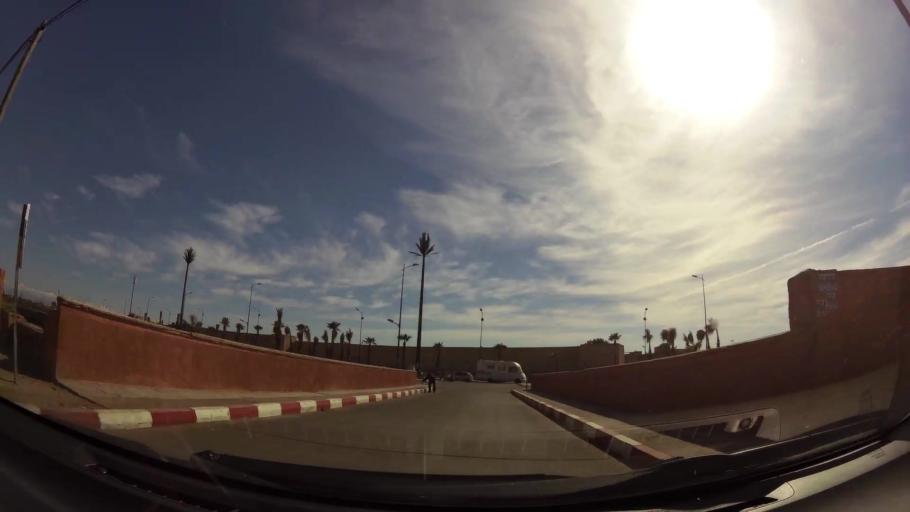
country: MA
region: Marrakech-Tensift-Al Haouz
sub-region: Marrakech
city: Marrakesh
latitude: 31.6389
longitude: -7.9804
